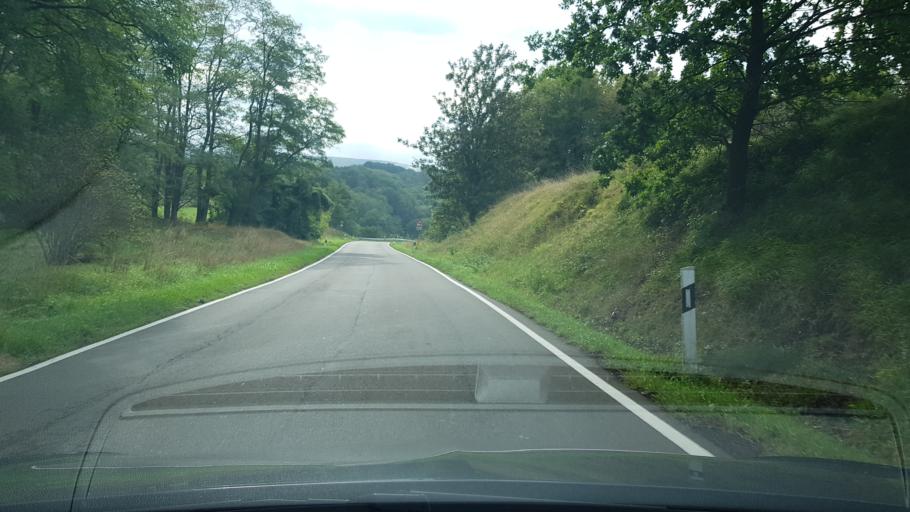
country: DE
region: Rheinland-Pfalz
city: Burgen
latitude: 50.2330
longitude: 7.3909
